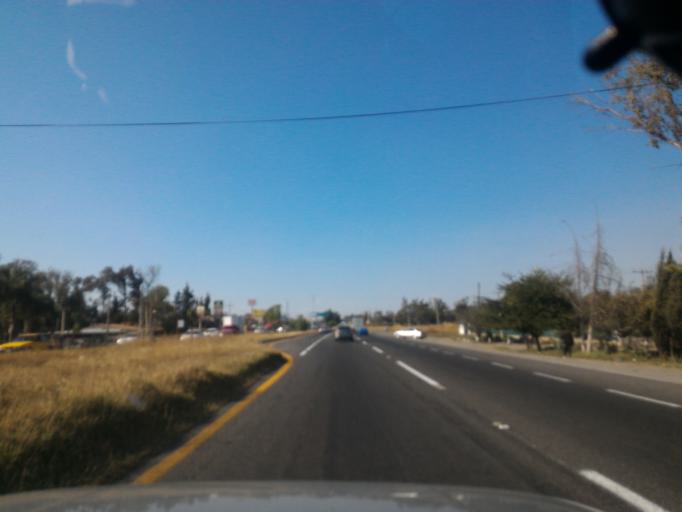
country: MX
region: Jalisco
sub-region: Tlajomulco de Zuniga
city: Rancho Alegre [Fraccionamiento]
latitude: 20.4635
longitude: -103.2561
